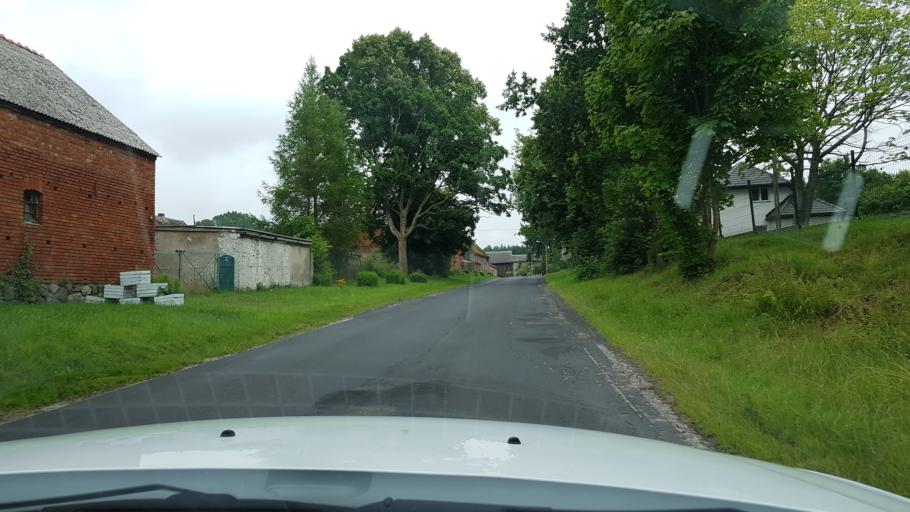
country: PL
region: West Pomeranian Voivodeship
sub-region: Powiat slawienski
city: Slawno
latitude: 54.4894
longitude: 16.5815
